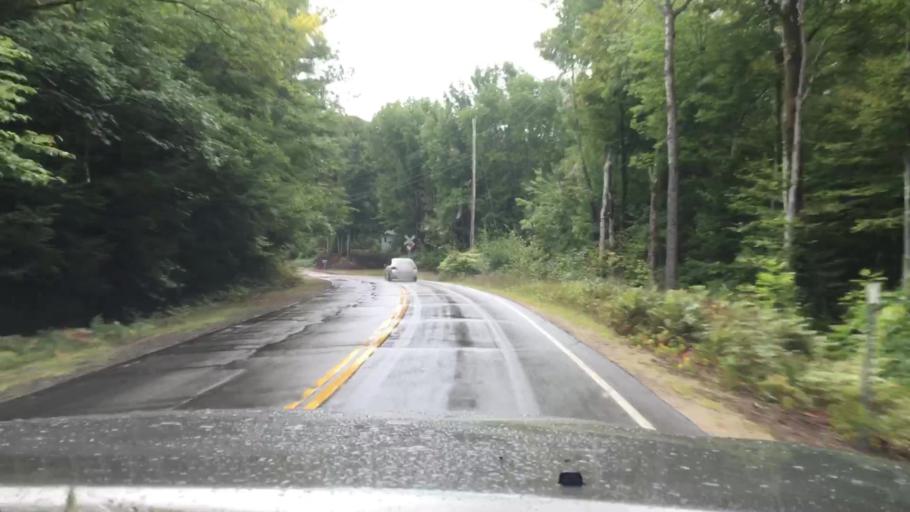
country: US
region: New Hampshire
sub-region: Belknap County
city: Meredith
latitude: 43.6626
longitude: -71.5460
